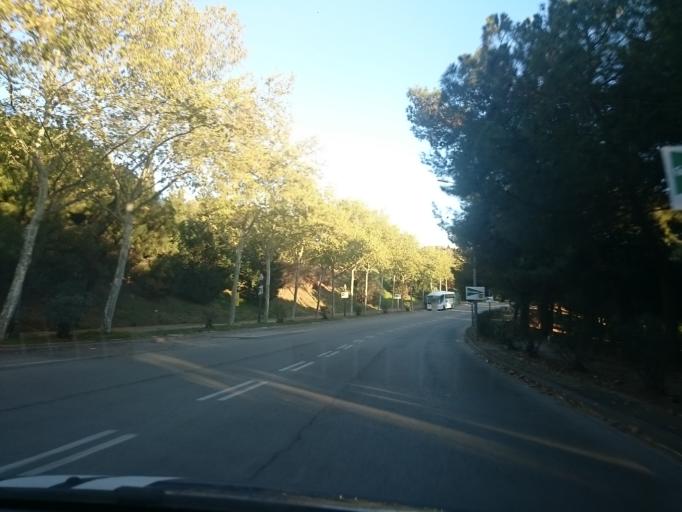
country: ES
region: Catalonia
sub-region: Provincia de Barcelona
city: Sants-Montjuic
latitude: 41.3618
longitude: 2.1484
